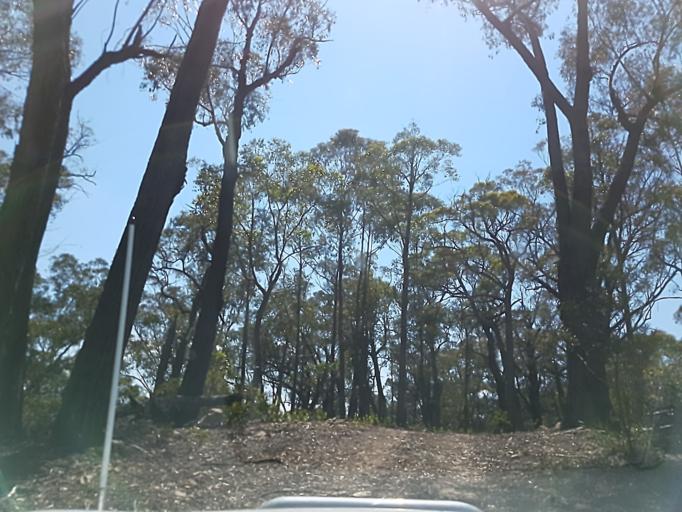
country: AU
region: Victoria
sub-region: East Gippsland
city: Lakes Entrance
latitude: -37.3116
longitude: 148.3483
